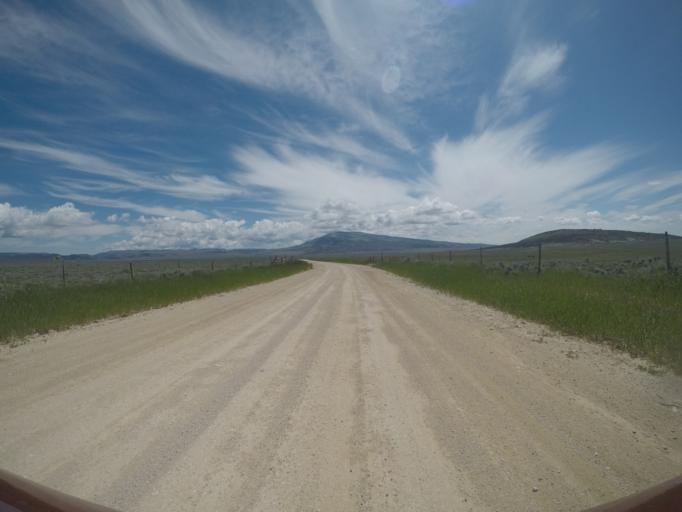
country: US
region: Wyoming
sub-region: Park County
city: Powell
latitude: 45.2053
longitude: -108.7606
